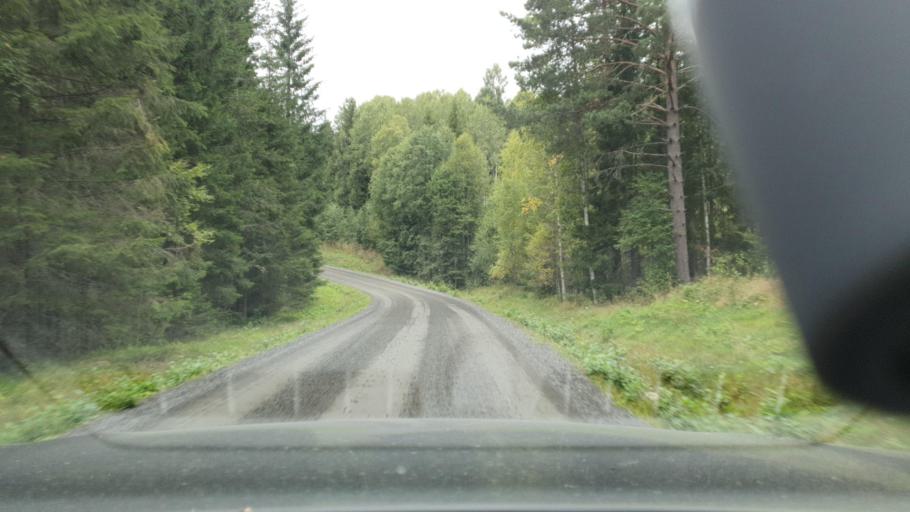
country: SE
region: Vaermland
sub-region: Torsby Kommun
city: Torsby
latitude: 60.3505
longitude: 12.8224
